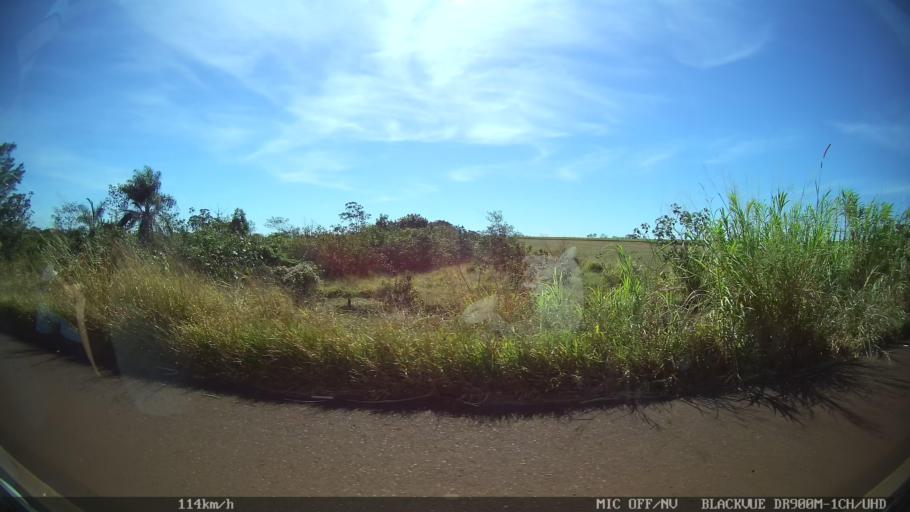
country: BR
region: Sao Paulo
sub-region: Nuporanga
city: Nuporanga
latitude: -20.5617
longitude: -47.6171
